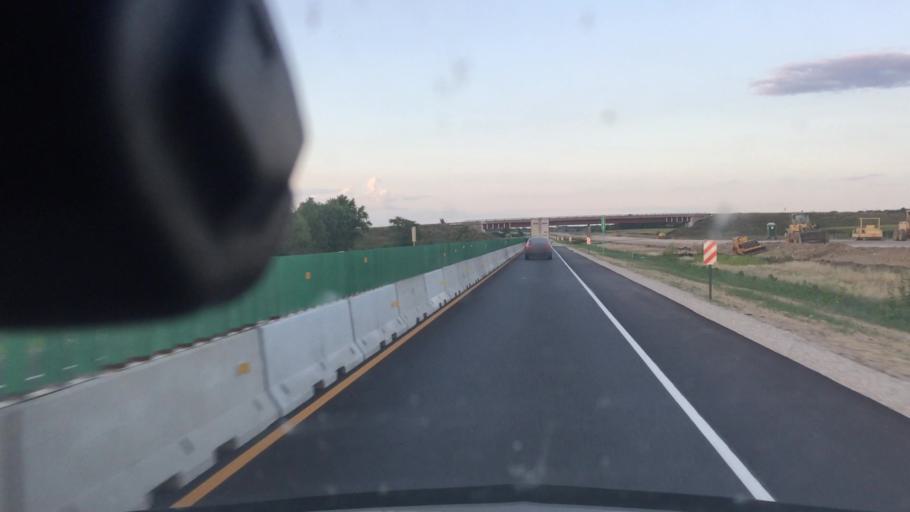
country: US
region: Illinois
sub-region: Livingston County
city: Pontiac
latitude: 40.9408
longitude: -88.5957
